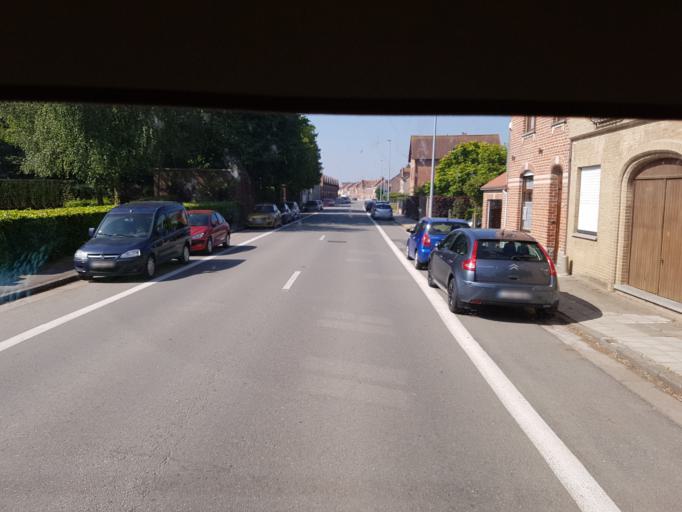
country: FR
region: Nord-Pas-de-Calais
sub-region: Departement du Nord
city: Deulemont
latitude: 50.7472
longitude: 2.9383
